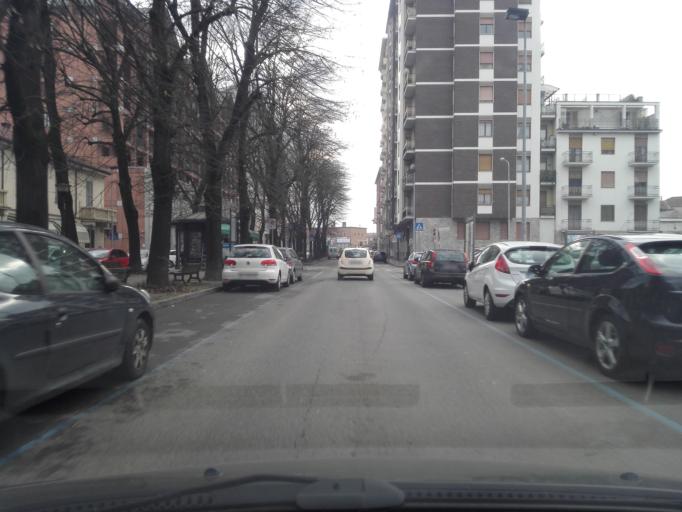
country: IT
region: Piedmont
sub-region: Provincia di Alessandria
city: Alessandria
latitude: 44.9120
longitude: 8.6076
